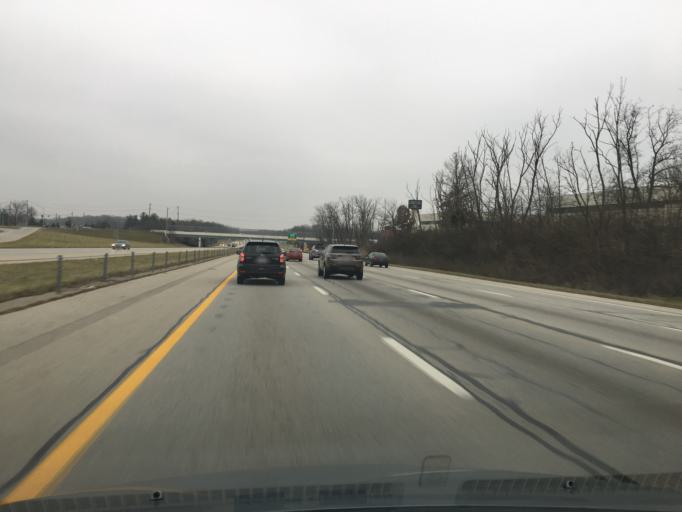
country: US
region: Ohio
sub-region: Hamilton County
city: Sixteen Mile Stand
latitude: 39.2635
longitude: -84.3412
